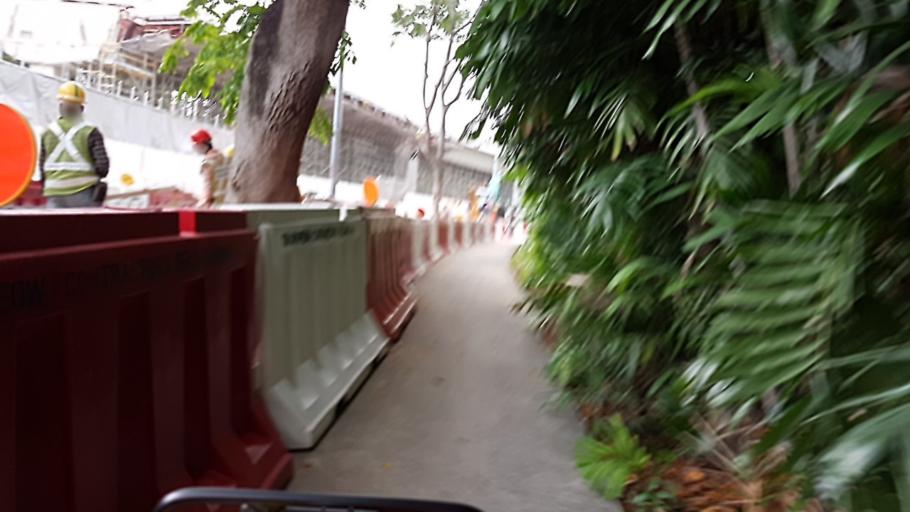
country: SG
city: Singapore
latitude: 1.3515
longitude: 103.9633
